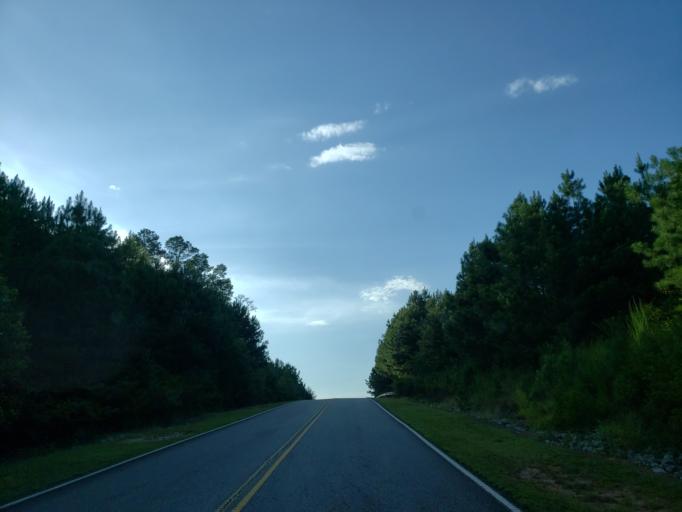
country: US
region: Georgia
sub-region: Cherokee County
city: Holly Springs
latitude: 34.2175
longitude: -84.5709
